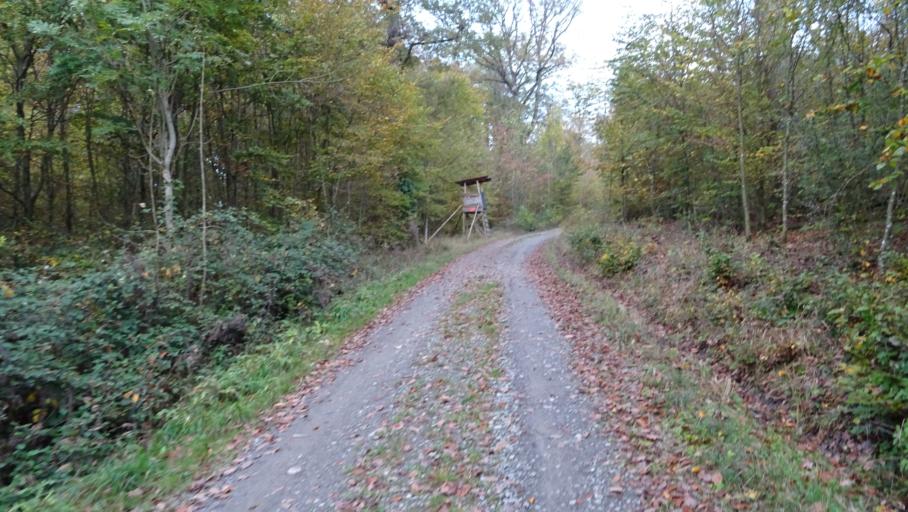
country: DE
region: Baden-Wuerttemberg
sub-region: Karlsruhe Region
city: Obrigheim
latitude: 49.3843
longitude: 9.0994
